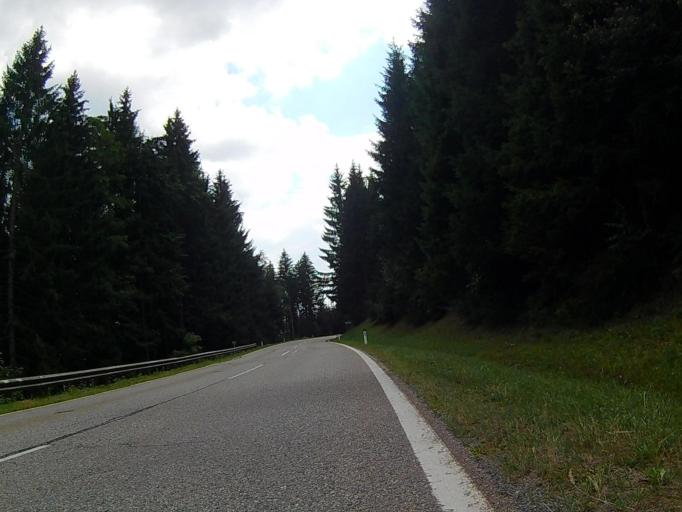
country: AT
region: Styria
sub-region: Politischer Bezirk Deutschlandsberg
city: Soboth
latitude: 46.6897
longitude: 15.1017
